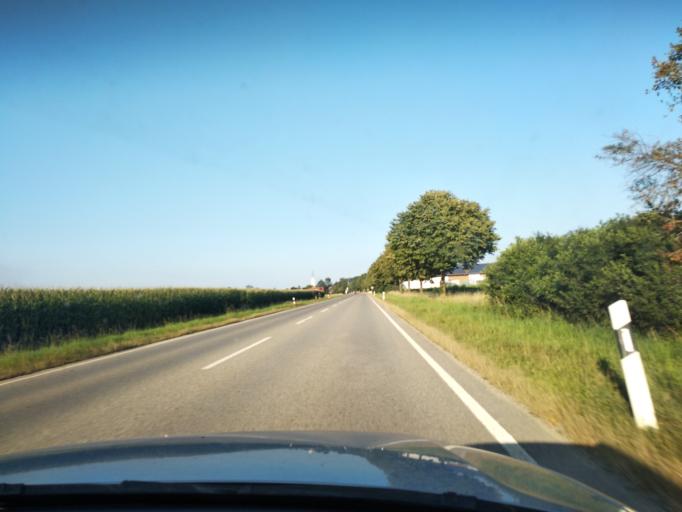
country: DE
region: Bavaria
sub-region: Upper Bavaria
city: Poing
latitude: 48.1464
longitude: 11.8076
